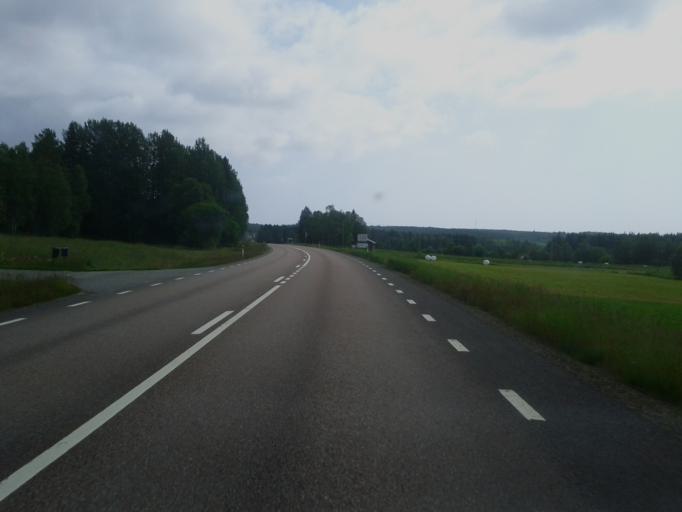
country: SE
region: Vaesterbotten
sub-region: Skelleftea Kommun
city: Burea
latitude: 64.3339
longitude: 21.2347
